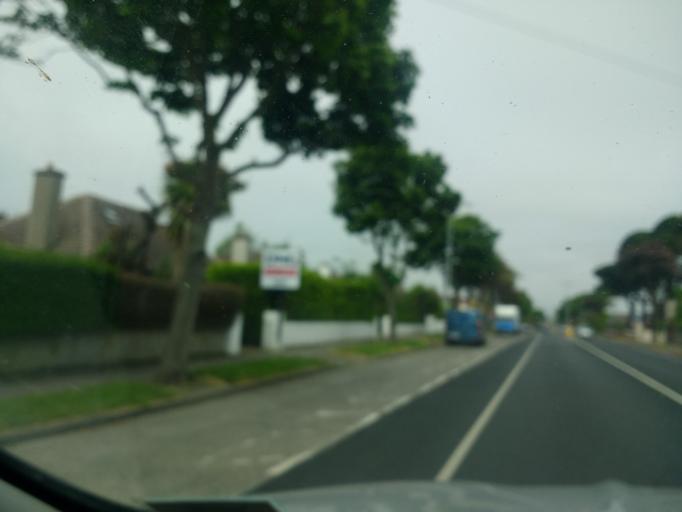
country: IE
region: Leinster
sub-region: Fingal County
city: Baldoyle
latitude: 53.3931
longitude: -6.1251
